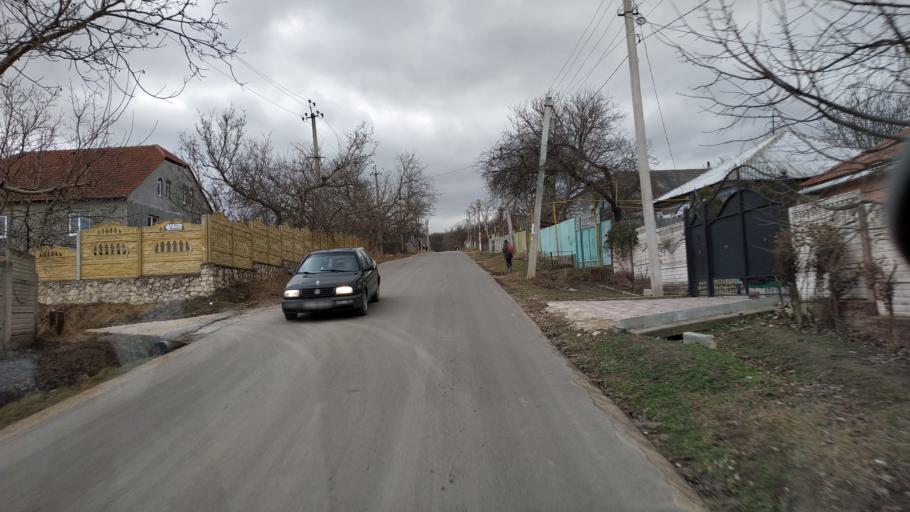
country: MD
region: Calarasi
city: Calarasi
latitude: 47.2433
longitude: 28.2836
